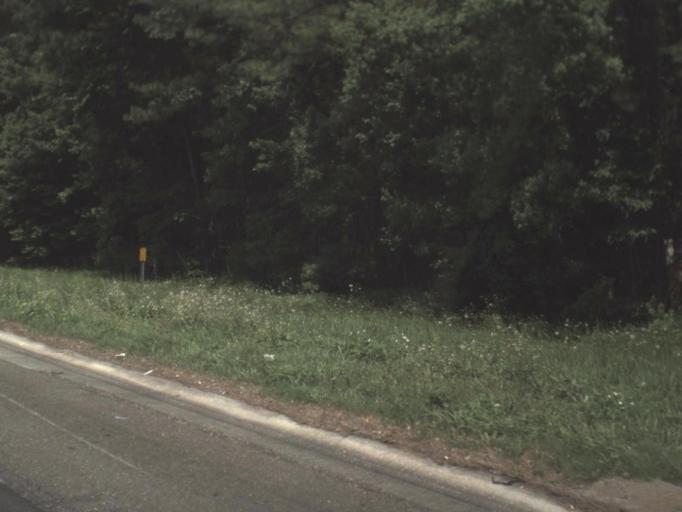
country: US
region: Florida
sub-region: Duval County
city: Jacksonville
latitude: 30.3643
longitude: -81.7608
